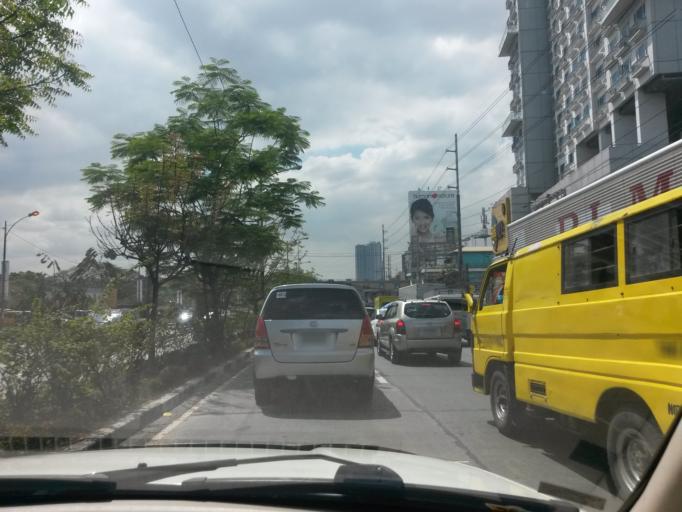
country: PH
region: Metro Manila
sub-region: Quezon City
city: Quezon City
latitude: 14.6453
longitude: 121.0745
